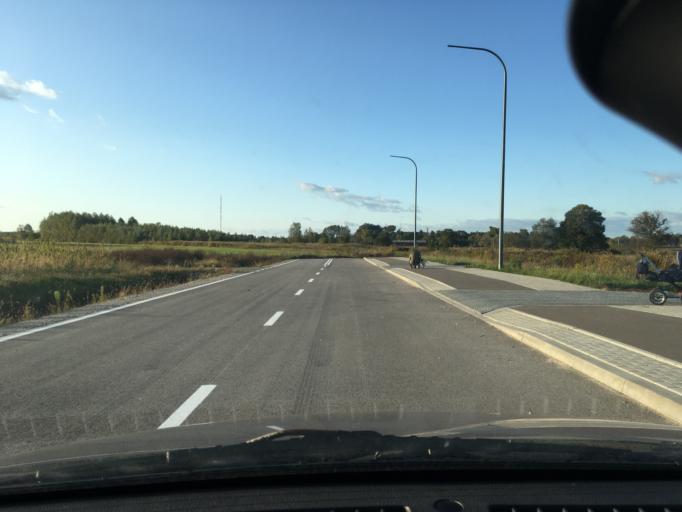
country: PL
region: Masovian Voivodeship
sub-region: Powiat piaseczynski
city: Lesznowola
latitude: 52.0471
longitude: 20.9250
